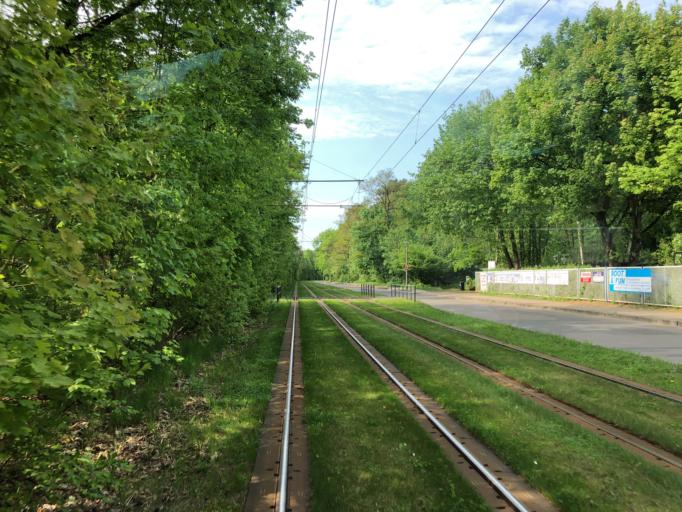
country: DE
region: Berlin
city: Schmockwitz
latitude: 52.3976
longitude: 13.6280
